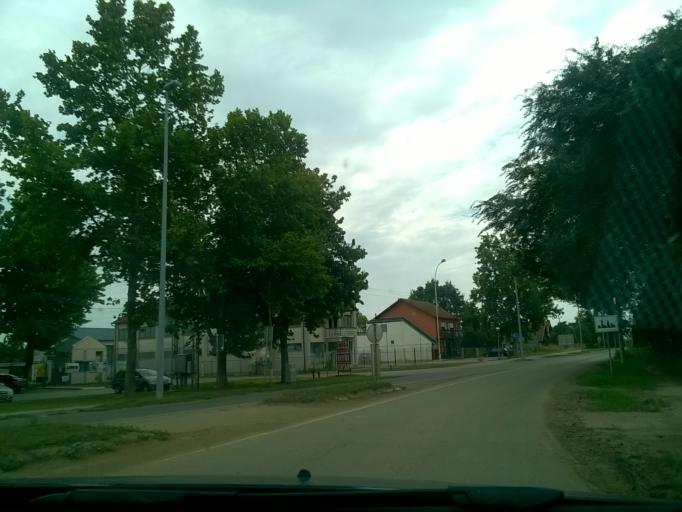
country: RS
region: Autonomna Pokrajina Vojvodina
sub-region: Srednjebanatski Okrug
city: Zrenjanin
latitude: 45.4017
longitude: 20.3930
